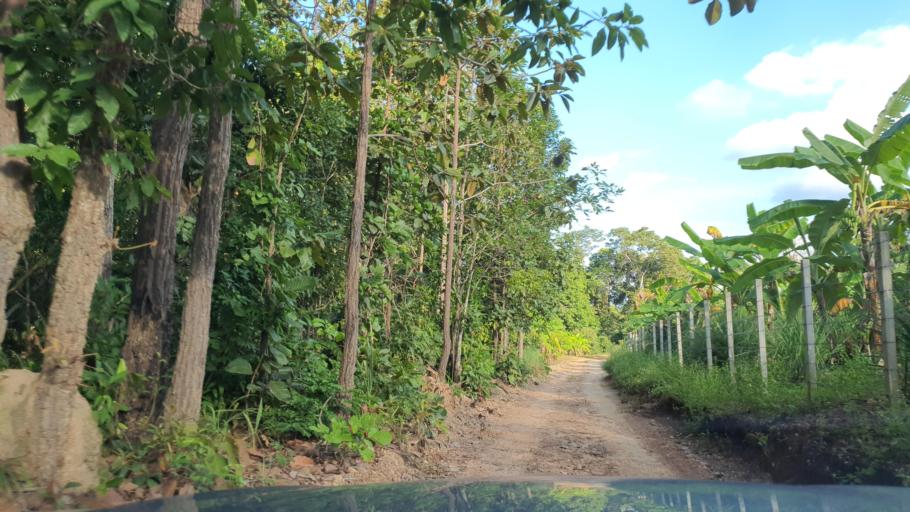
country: TH
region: Chiang Mai
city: Hang Dong
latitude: 18.7217
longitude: 98.8520
